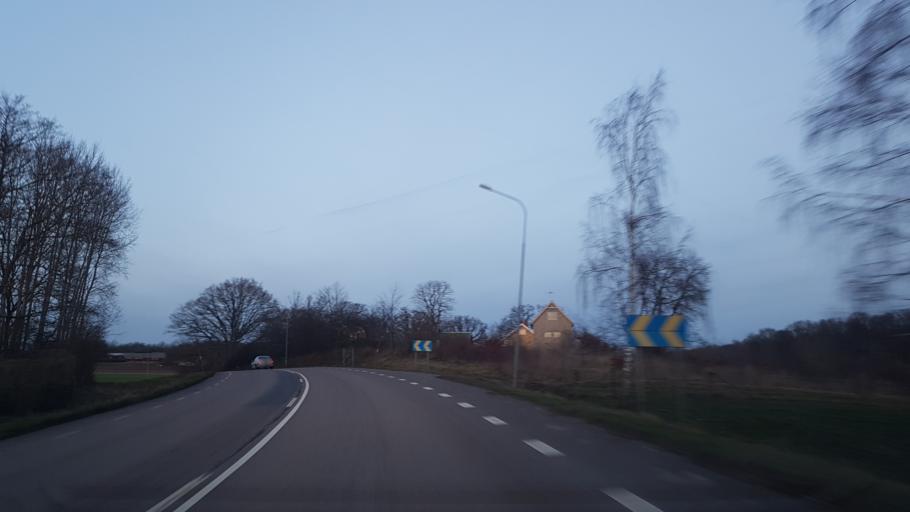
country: SE
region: Blekinge
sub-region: Karlskrona Kommun
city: Jaemjoe
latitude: 56.1734
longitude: 15.8358
